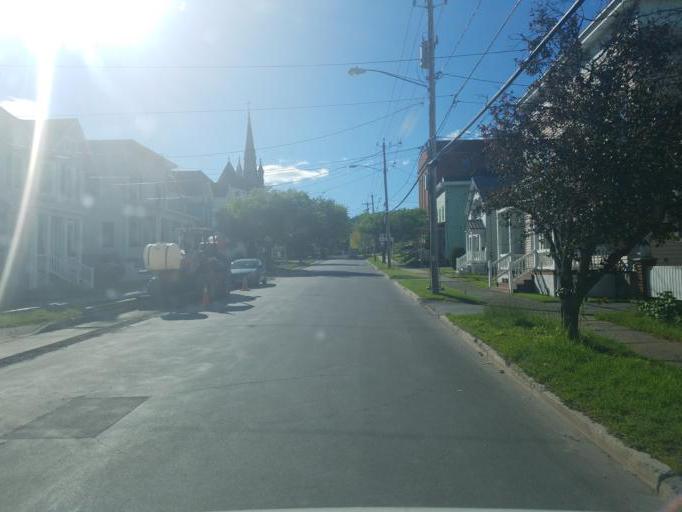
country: US
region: New York
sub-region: Herkimer County
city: Little Falls
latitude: 43.0432
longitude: -74.8510
